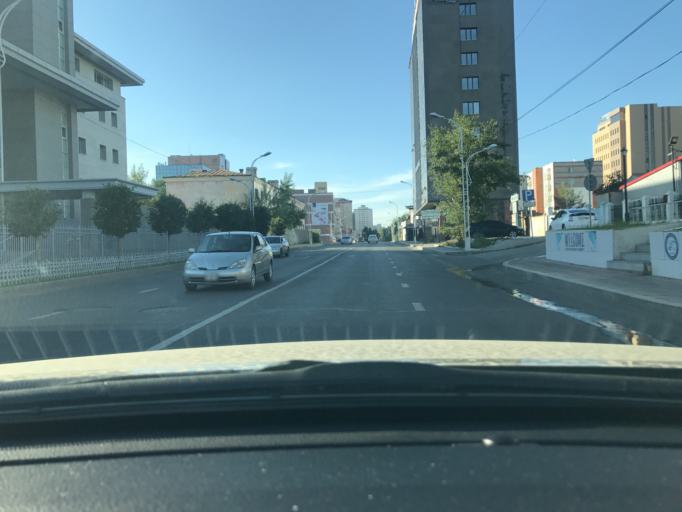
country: MN
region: Ulaanbaatar
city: Ulaanbaatar
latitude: 47.9197
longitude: 106.9352
